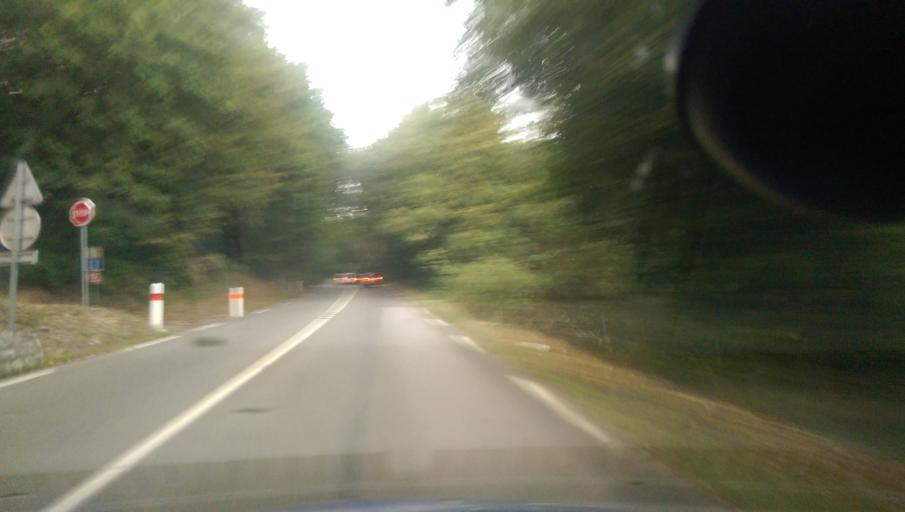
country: FR
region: Provence-Alpes-Cote d'Azur
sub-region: Departement des Alpes-Maritimes
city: Opio
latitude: 43.6730
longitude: 6.9816
